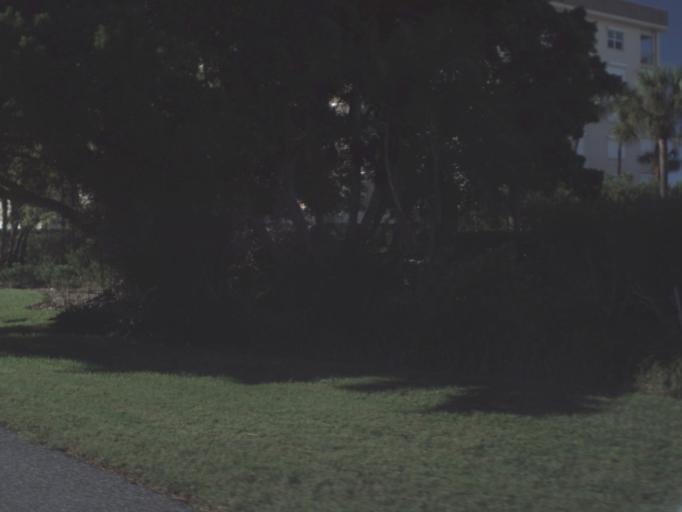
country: US
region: Florida
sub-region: Manatee County
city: Longboat Key
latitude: 27.3933
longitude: -82.6439
